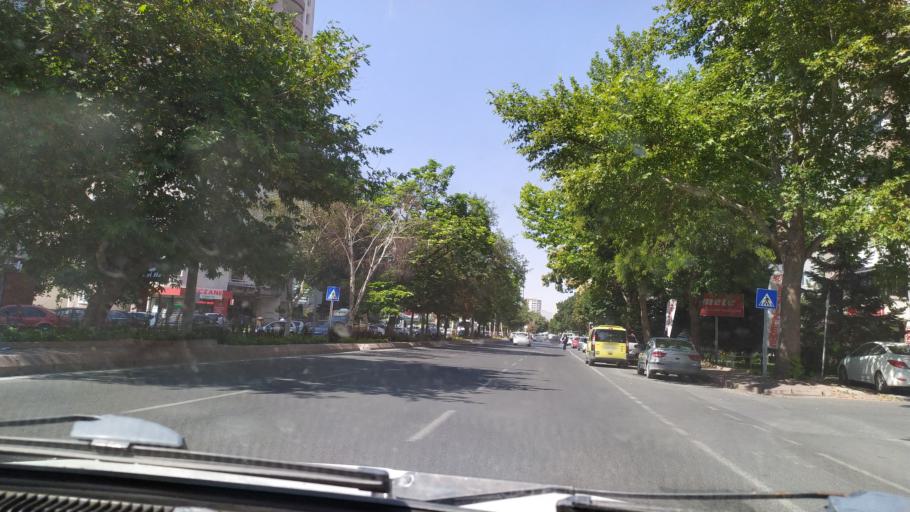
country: TR
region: Kayseri
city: Kayseri
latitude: 38.7260
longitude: 35.5198
